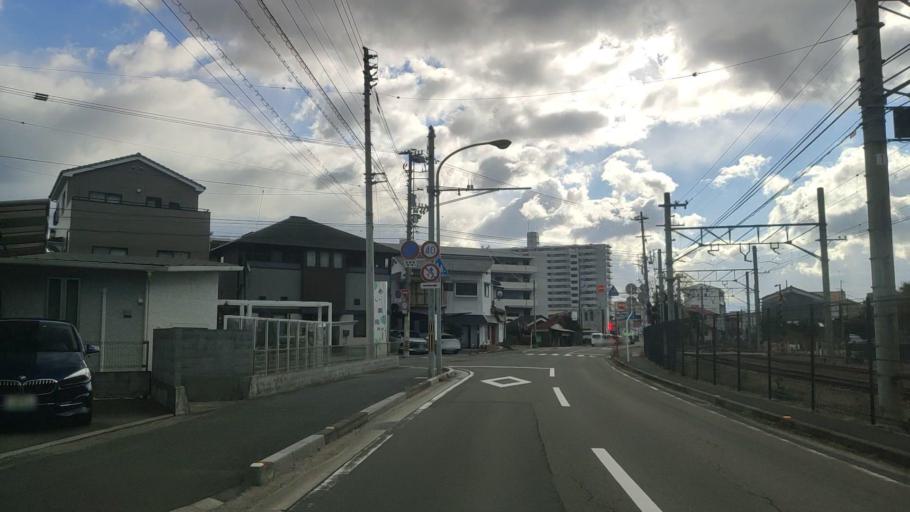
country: JP
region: Ehime
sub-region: Shikoku-chuo Shi
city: Matsuyama
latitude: 33.8690
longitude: 132.7170
